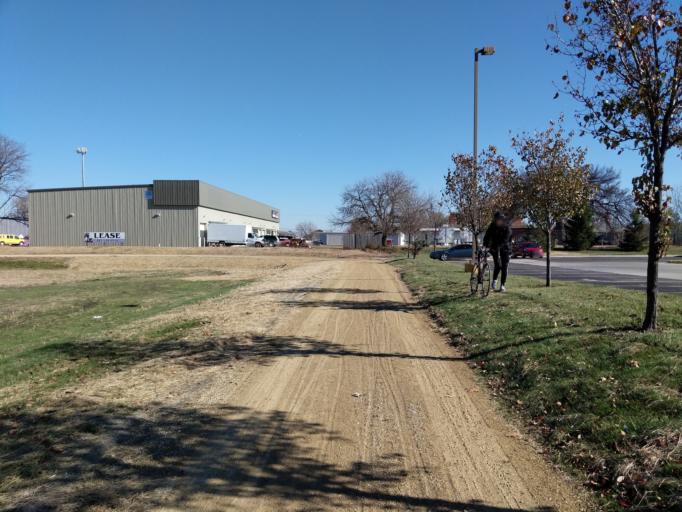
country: US
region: Kansas
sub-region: Riley County
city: Manhattan
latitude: 39.1908
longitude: -96.5591
